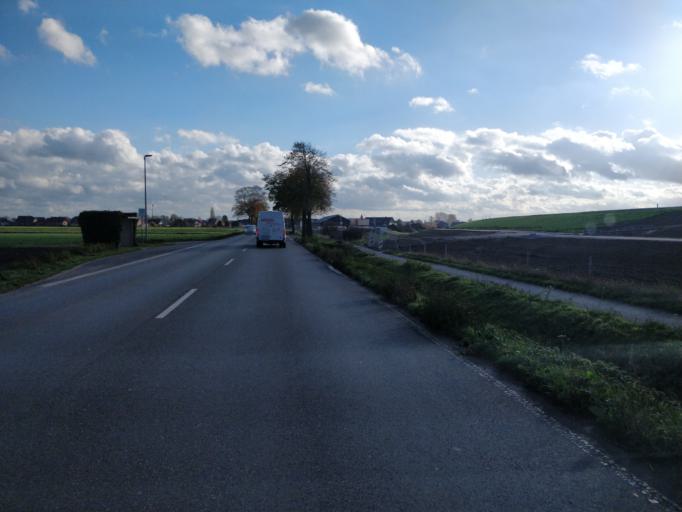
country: DE
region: North Rhine-Westphalia
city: Rees
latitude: 51.8086
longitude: 6.3657
